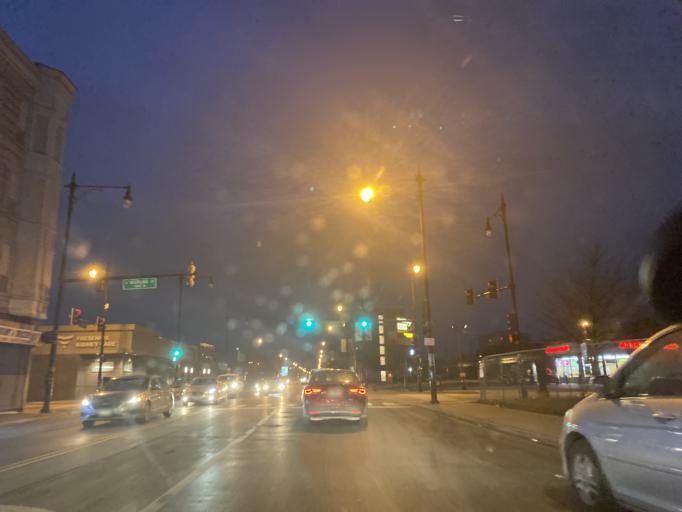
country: US
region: Illinois
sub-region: Cook County
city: Chicago
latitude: 41.7797
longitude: -87.6500
